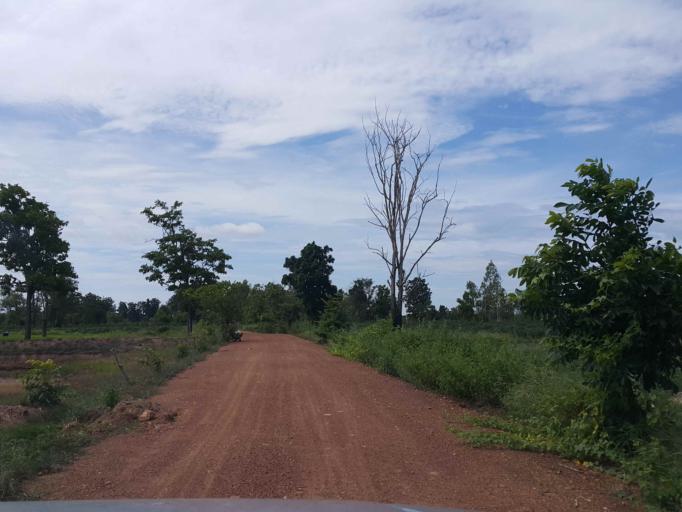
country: TH
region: Sukhothai
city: Ban Dan Lan Hoi
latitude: 17.0997
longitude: 99.4680
